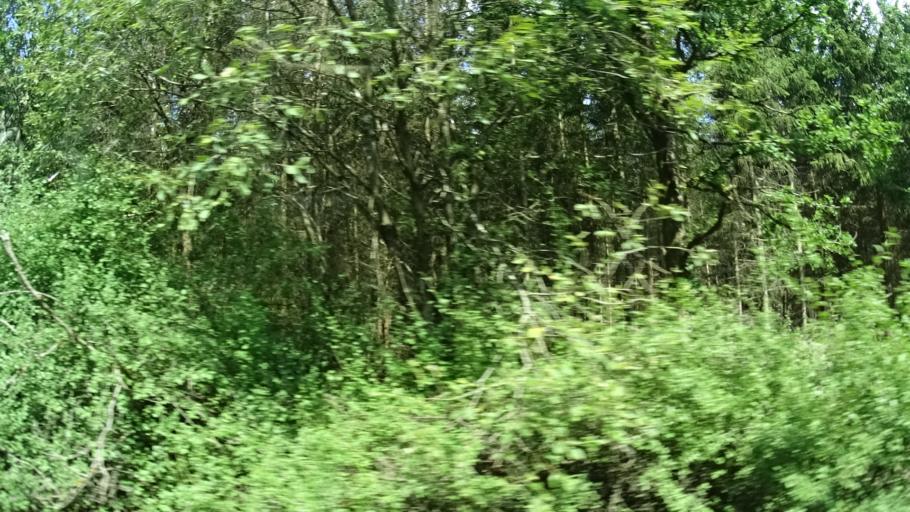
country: DE
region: Thuringia
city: Veilsdorf
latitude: 50.3944
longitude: 10.7752
